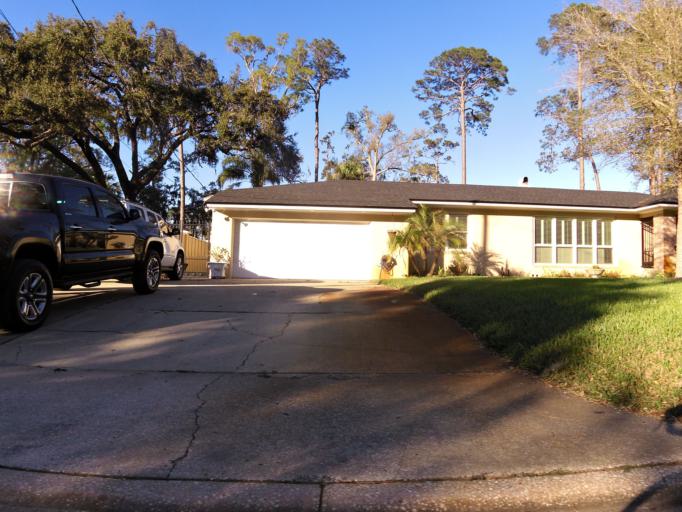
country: US
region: Florida
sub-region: Duval County
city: Jacksonville
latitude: 30.2468
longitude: -81.6347
